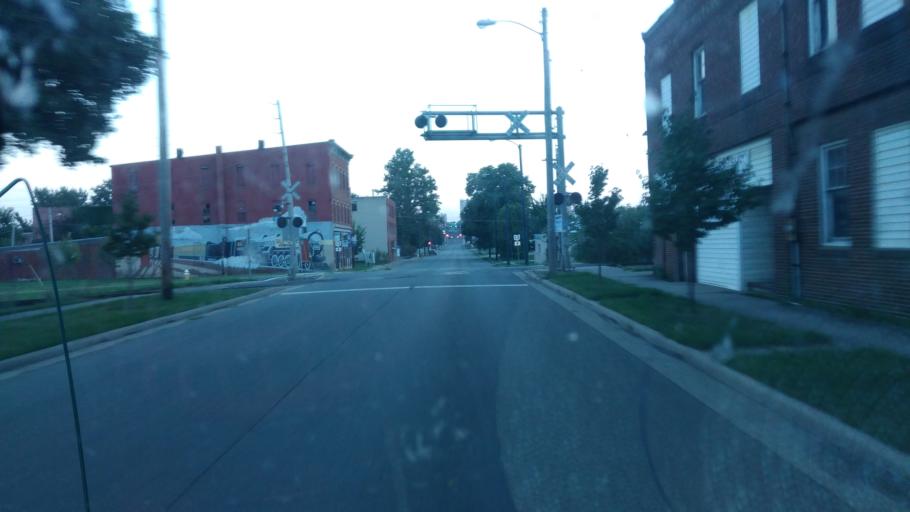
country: US
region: Ohio
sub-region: Richland County
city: Mansfield
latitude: 40.7671
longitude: -82.5150
